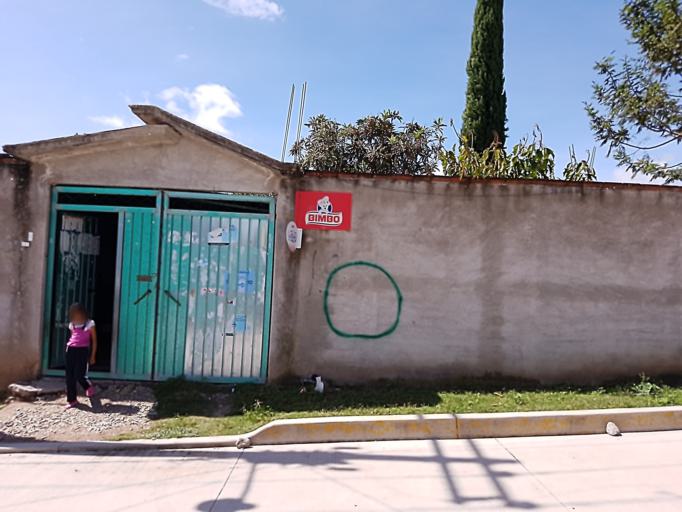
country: MX
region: Oaxaca
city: Ciudad de Huajuapam de Leon
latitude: 17.8037
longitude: -97.7938
